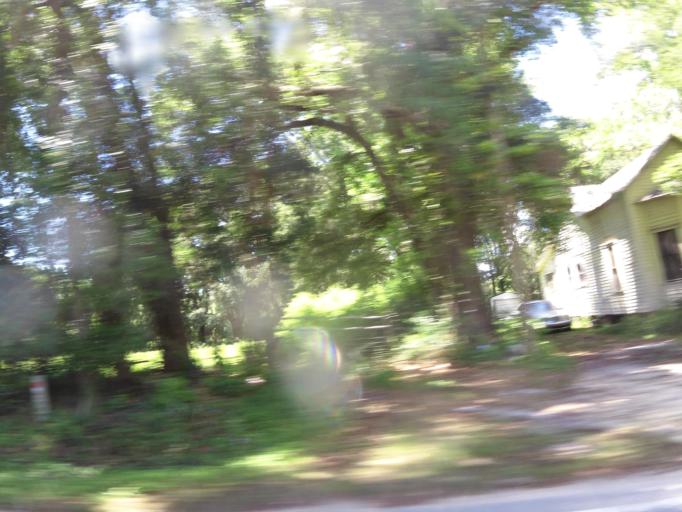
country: US
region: Florida
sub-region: Union County
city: Lake Butler
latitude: 30.0604
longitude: -82.2366
